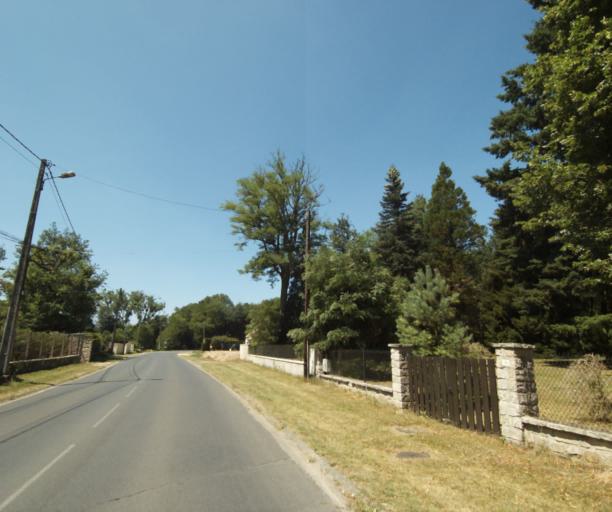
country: FR
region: Ile-de-France
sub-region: Departement de Seine-et-Marne
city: Noisy-sur-Ecole
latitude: 48.3639
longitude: 2.5190
